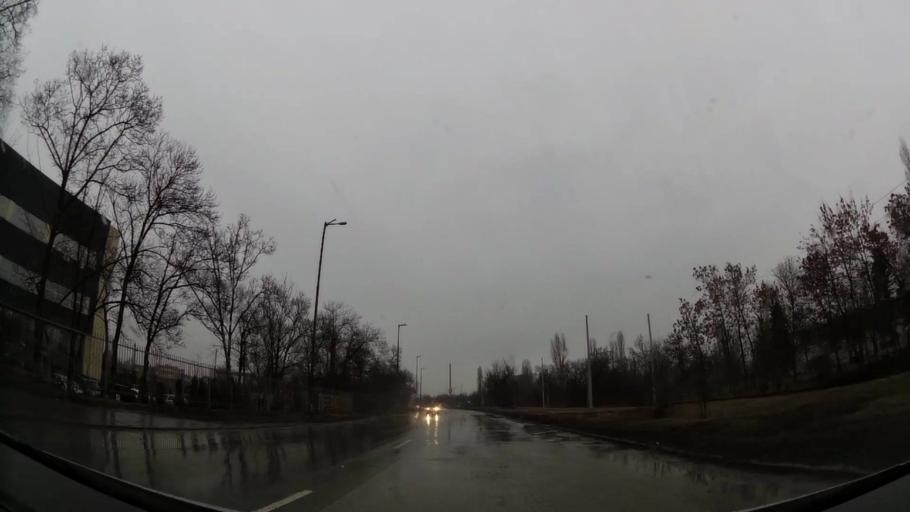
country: BG
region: Sofia-Capital
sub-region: Stolichna Obshtina
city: Sofia
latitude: 42.6650
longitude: 23.4083
